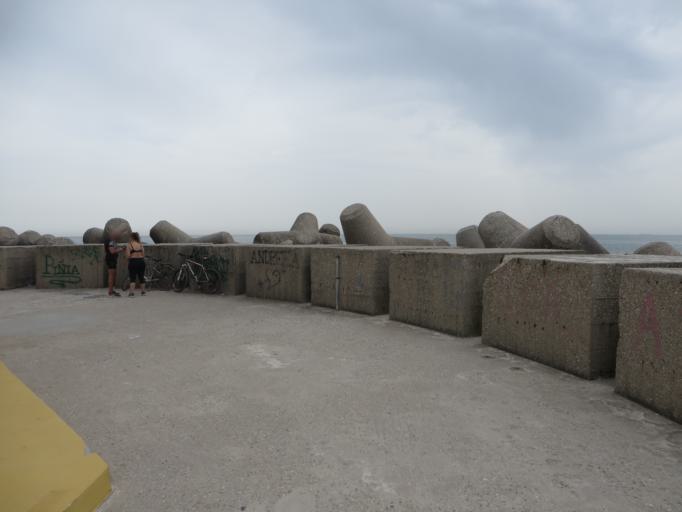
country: IT
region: Veneto
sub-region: Provincia di Venezia
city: Ca' Savio
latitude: 45.4227
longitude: 12.4366
